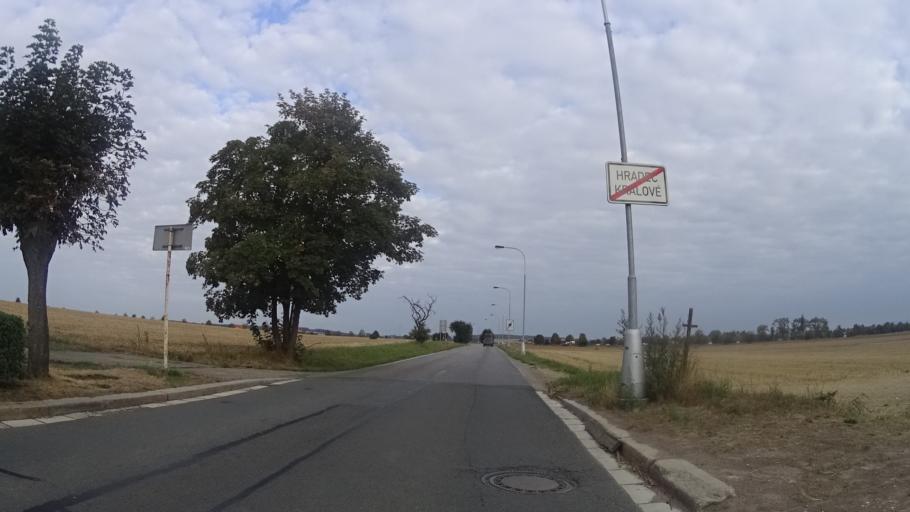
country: CZ
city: Stezery
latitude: 50.2080
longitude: 15.7873
